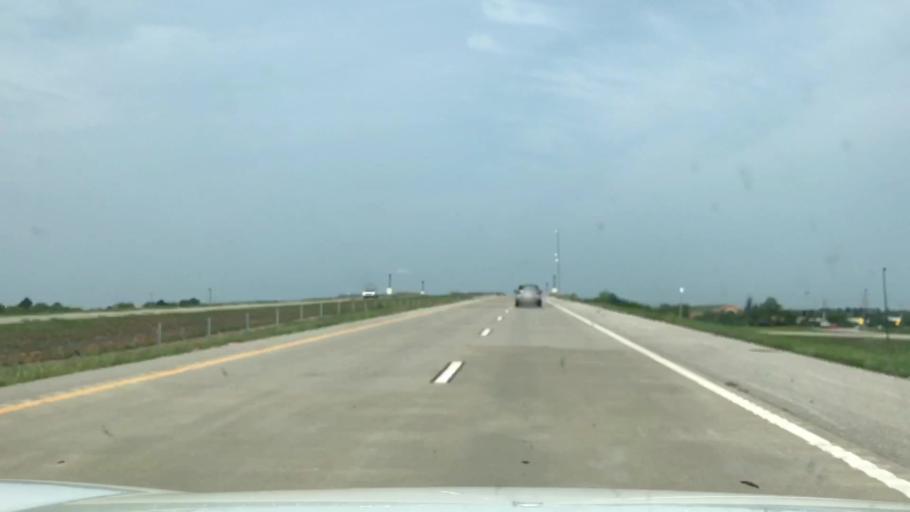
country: US
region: Missouri
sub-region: Saint Charles County
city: Dardenne Prairie
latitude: 38.7529
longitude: -90.6977
